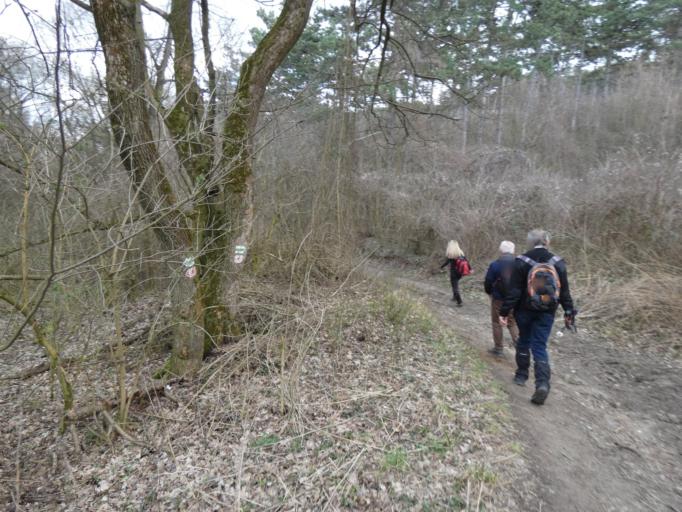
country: HU
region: Pest
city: Pilisborosjeno
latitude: 47.6203
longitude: 19.0073
